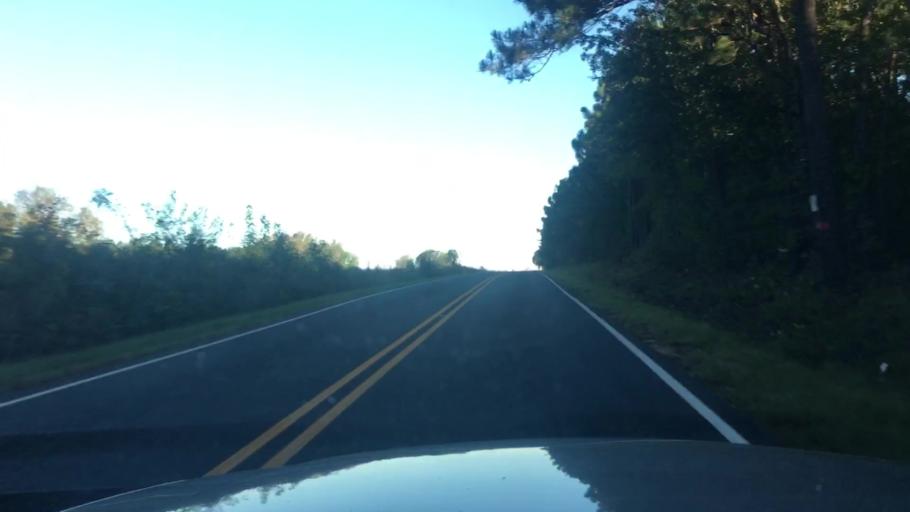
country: US
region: North Carolina
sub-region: Harnett County
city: Walkertown
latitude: 35.2798
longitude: -78.8661
